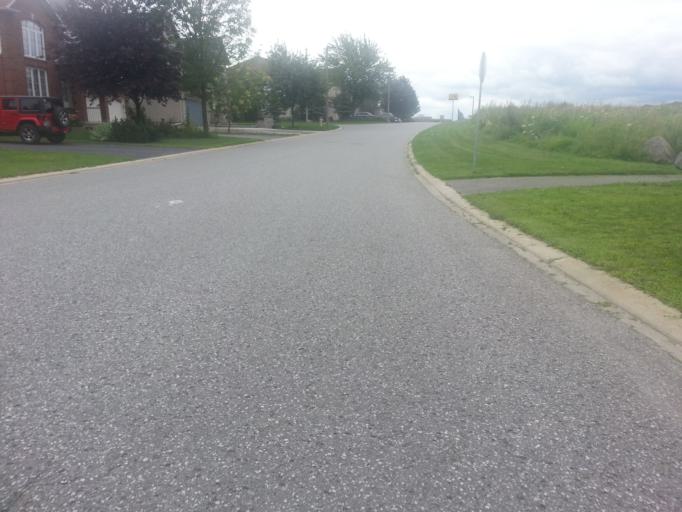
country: CA
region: Ontario
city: Bells Corners
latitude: 45.3258
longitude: -75.9269
